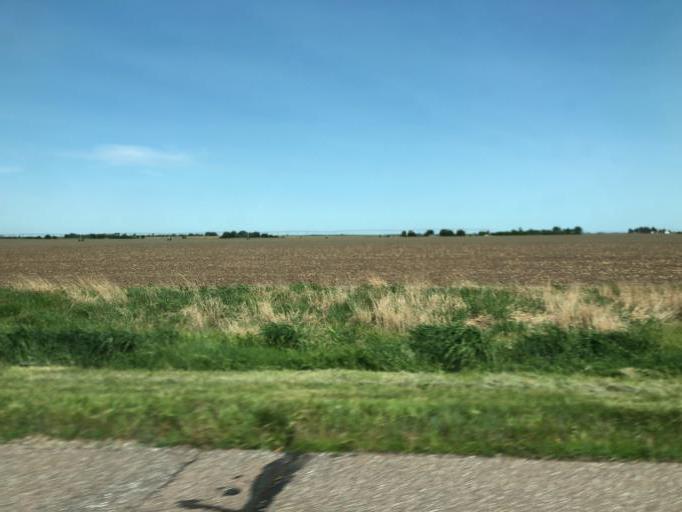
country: US
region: Nebraska
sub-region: Fillmore County
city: Geneva
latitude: 40.6721
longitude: -97.5957
